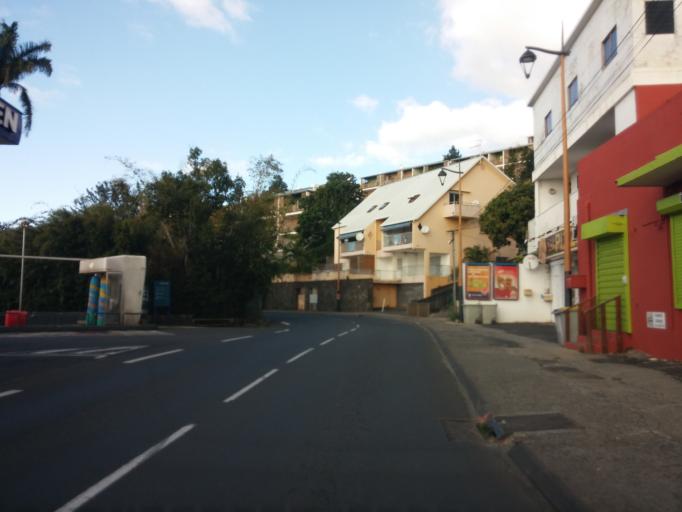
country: RE
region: Reunion
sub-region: Reunion
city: Saint-Denis
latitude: -20.8911
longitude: 55.4215
